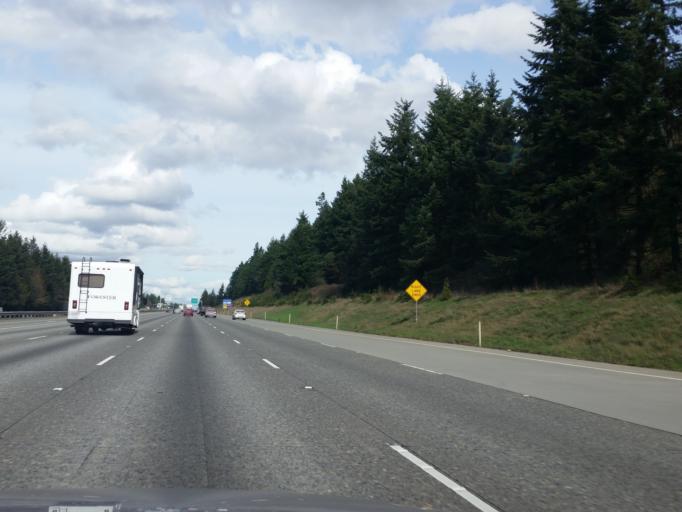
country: US
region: Washington
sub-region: King County
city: Lakeland South
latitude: 47.2952
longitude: -122.3045
